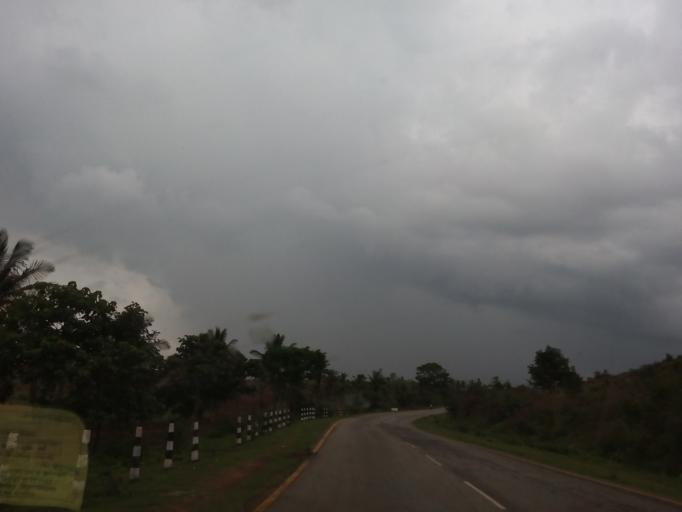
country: IN
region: Karnataka
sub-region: Hassan
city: Hassan
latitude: 13.0885
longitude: 76.0380
